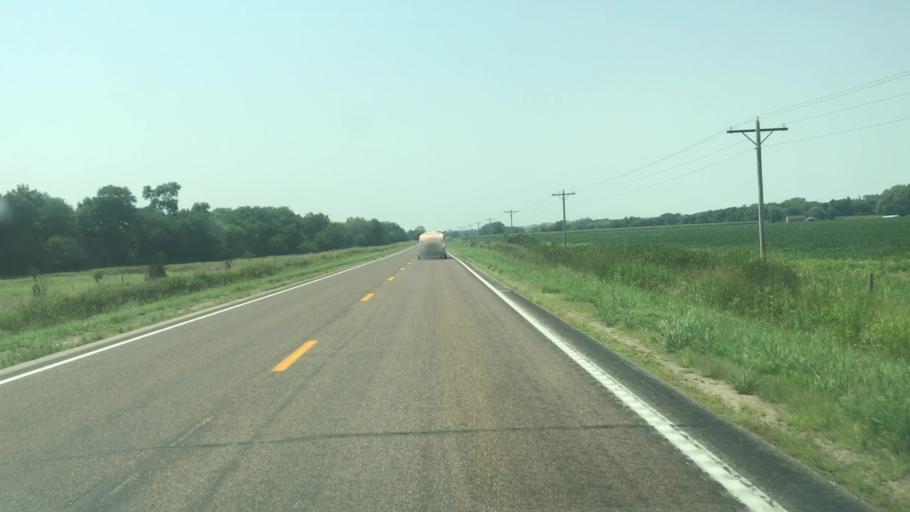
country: US
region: Nebraska
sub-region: Buffalo County
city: Ravenna
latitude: 41.0760
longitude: -98.6732
